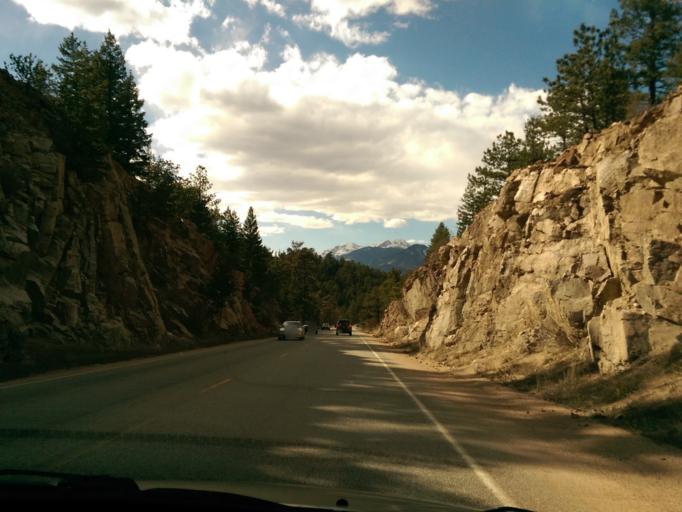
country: US
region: Colorado
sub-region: Larimer County
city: Estes Park
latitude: 40.3627
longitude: -105.4682
